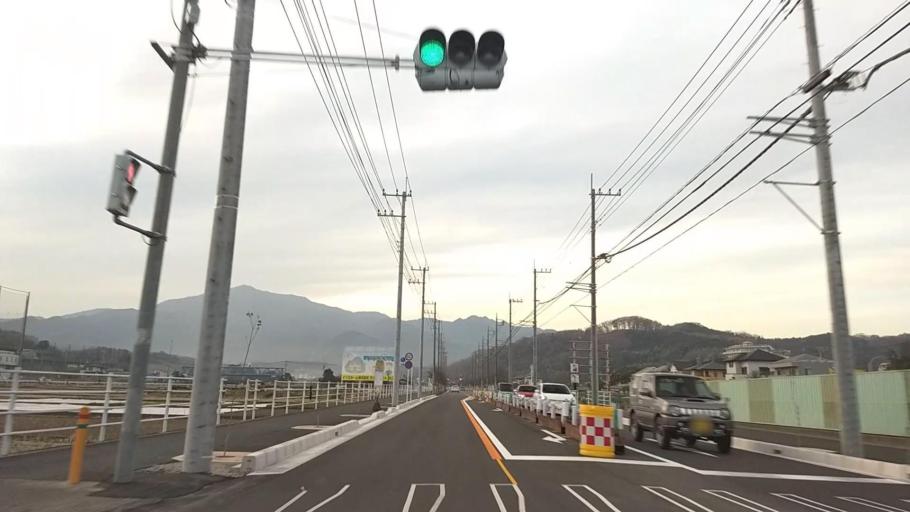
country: JP
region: Kanagawa
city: Atsugi
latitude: 35.4317
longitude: 139.3276
